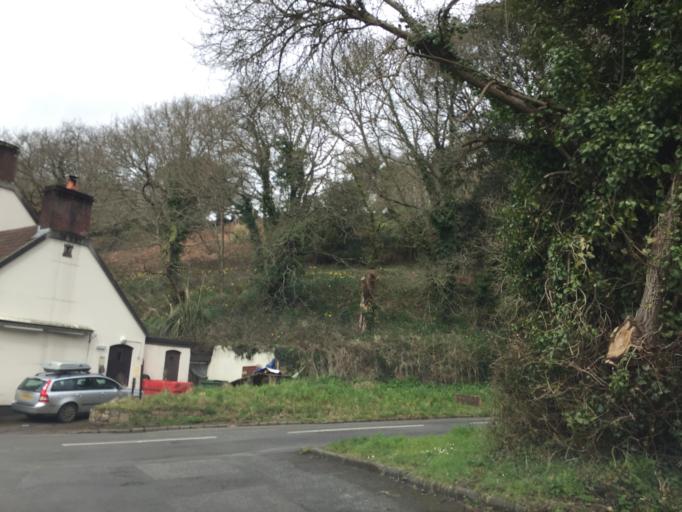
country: JE
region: St Helier
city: Saint Helier
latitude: 49.2110
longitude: -2.1608
